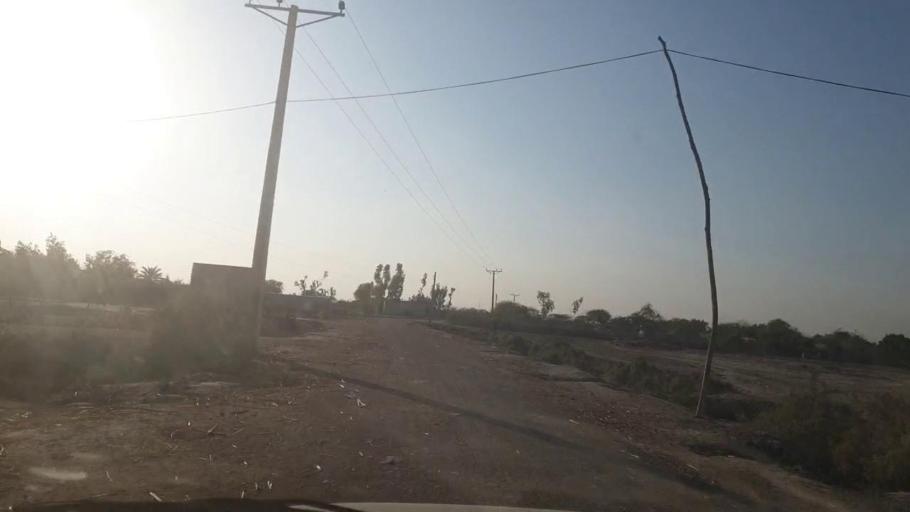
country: PK
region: Sindh
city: Mirpur Khas
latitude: 25.4618
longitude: 69.1085
